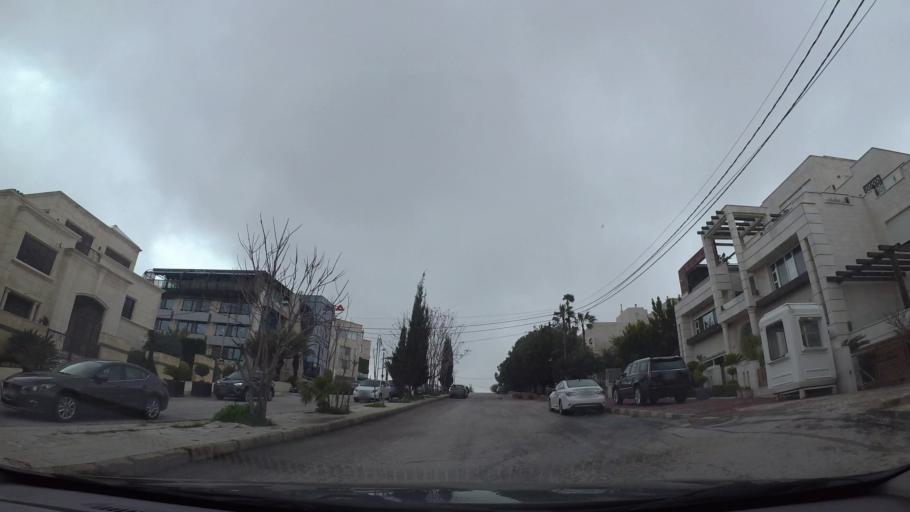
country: JO
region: Amman
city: Al Bunayyat ash Shamaliyah
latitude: 31.9362
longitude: 35.8924
